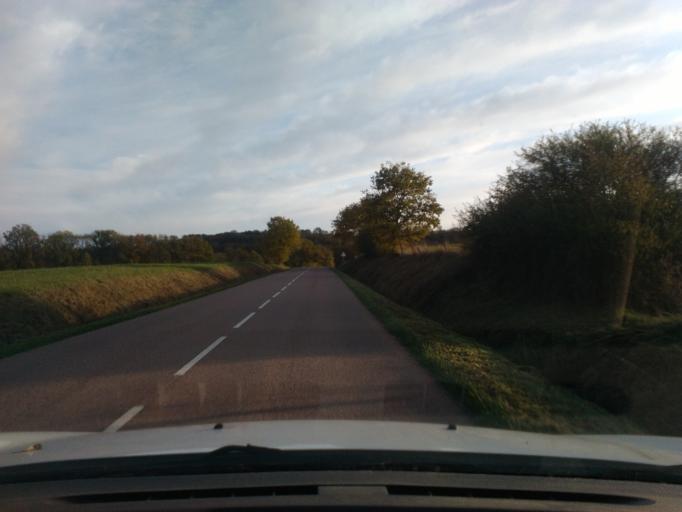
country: FR
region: Lorraine
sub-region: Departement des Vosges
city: Mirecourt
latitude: 48.2202
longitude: 6.1558
